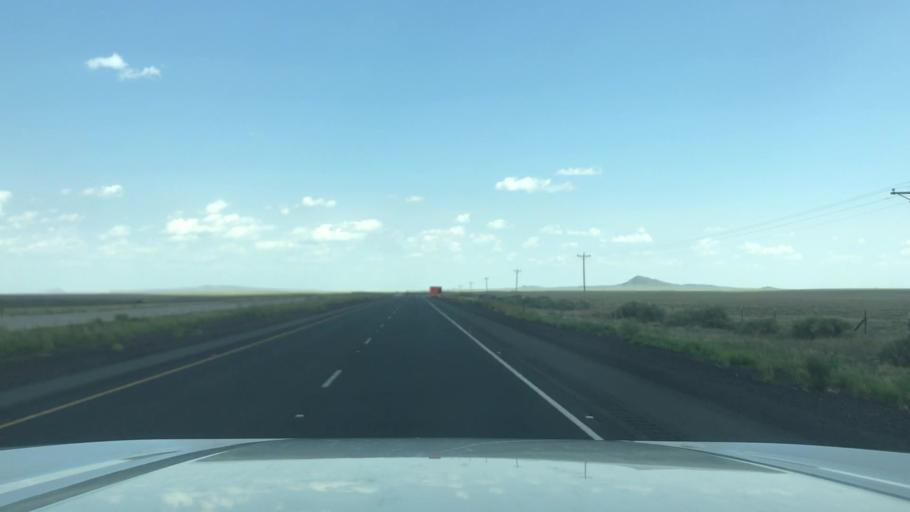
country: US
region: New Mexico
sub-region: Union County
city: Clayton
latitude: 36.6310
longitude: -103.7134
